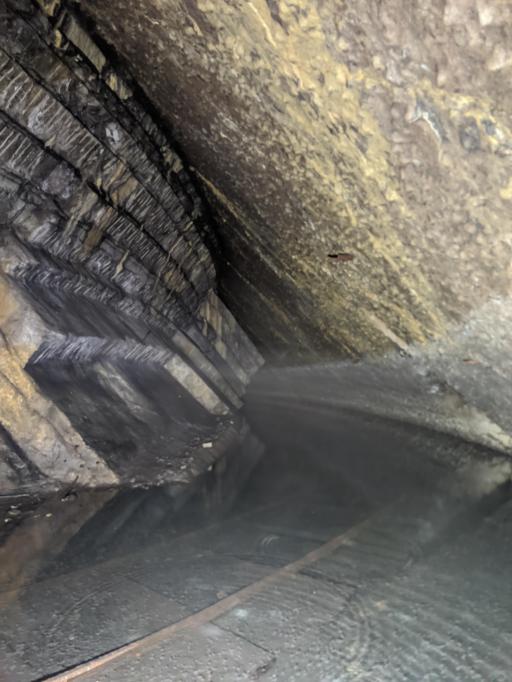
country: BE
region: Wallonia
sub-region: Province de Namur
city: Anhee
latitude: 50.3178
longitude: 4.8305
